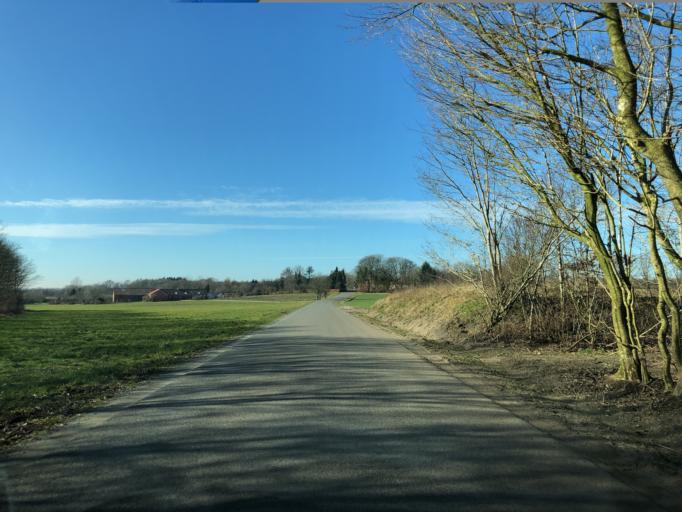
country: DK
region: Central Jutland
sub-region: Ikast-Brande Kommune
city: Bording Kirkeby
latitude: 56.1554
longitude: 9.2403
